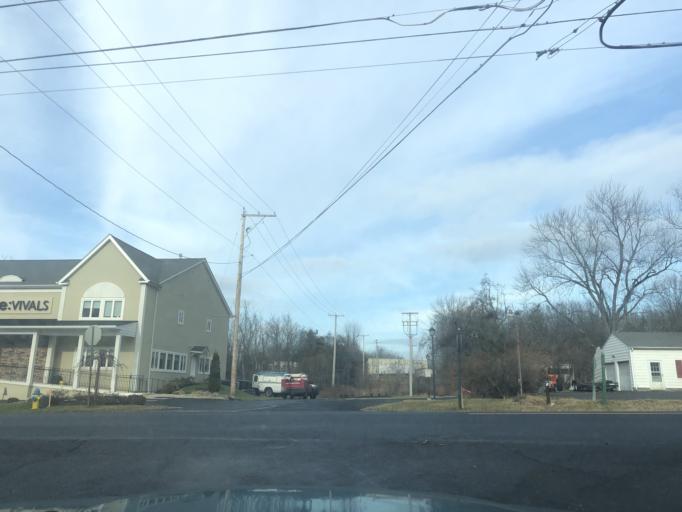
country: US
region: Pennsylvania
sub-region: Bucks County
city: Perkasie
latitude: 40.3778
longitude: -75.3034
